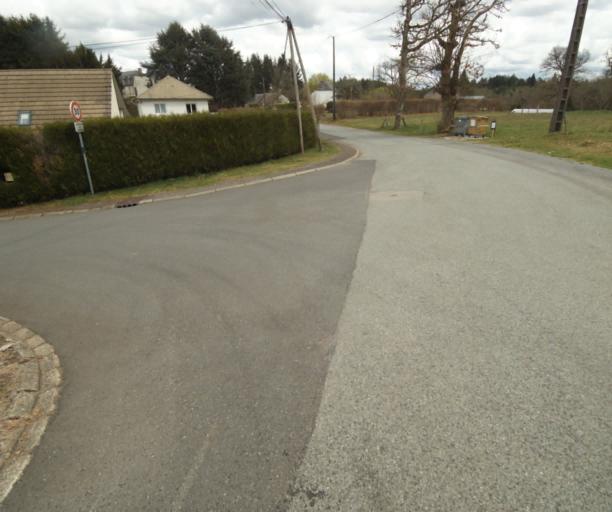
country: FR
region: Limousin
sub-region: Departement de la Correze
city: Correze
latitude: 45.3336
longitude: 1.9439
